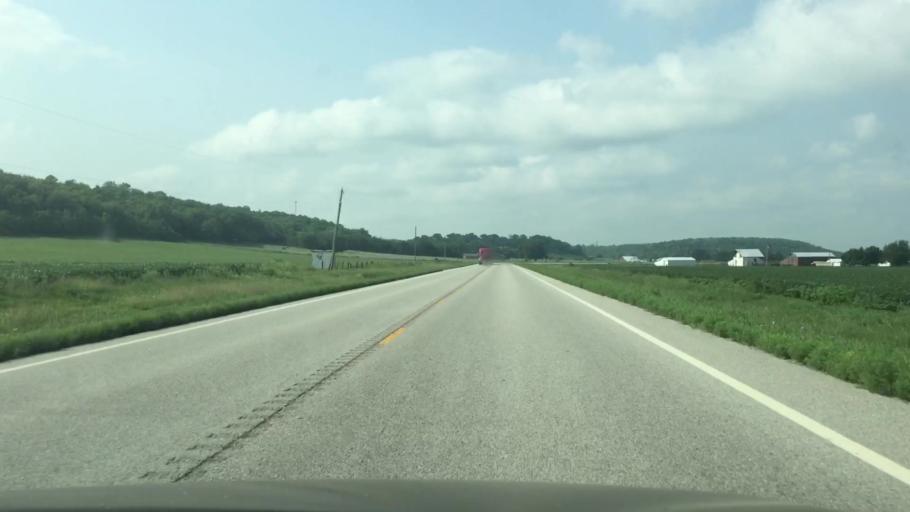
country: US
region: Kansas
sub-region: Anderson County
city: Garnett
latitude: 38.3670
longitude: -95.1181
